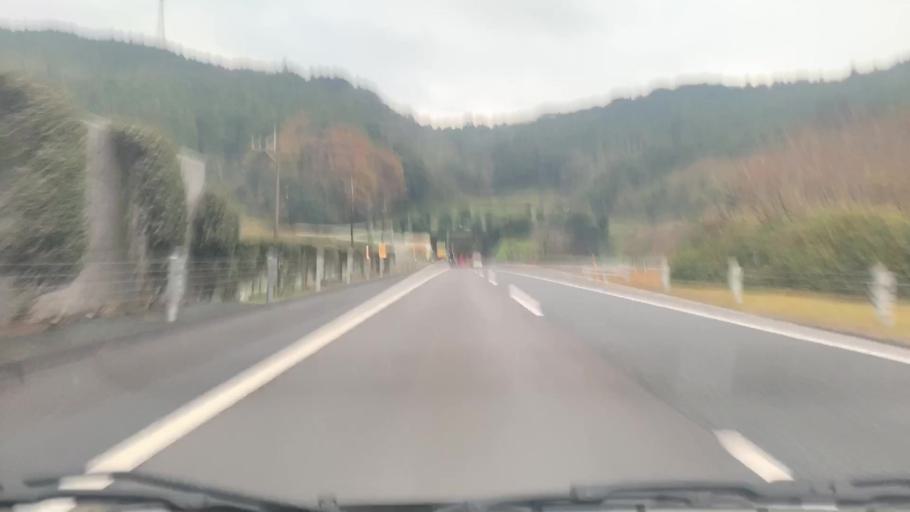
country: JP
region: Nagasaki
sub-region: Isahaya-shi
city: Isahaya
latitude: 32.8753
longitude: 129.9976
